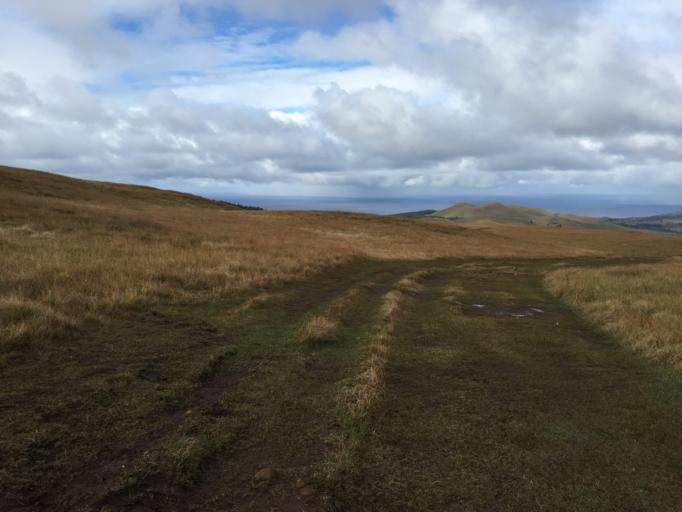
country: CL
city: Ostrov Paskhi
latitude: -27.0936
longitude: -109.3810
